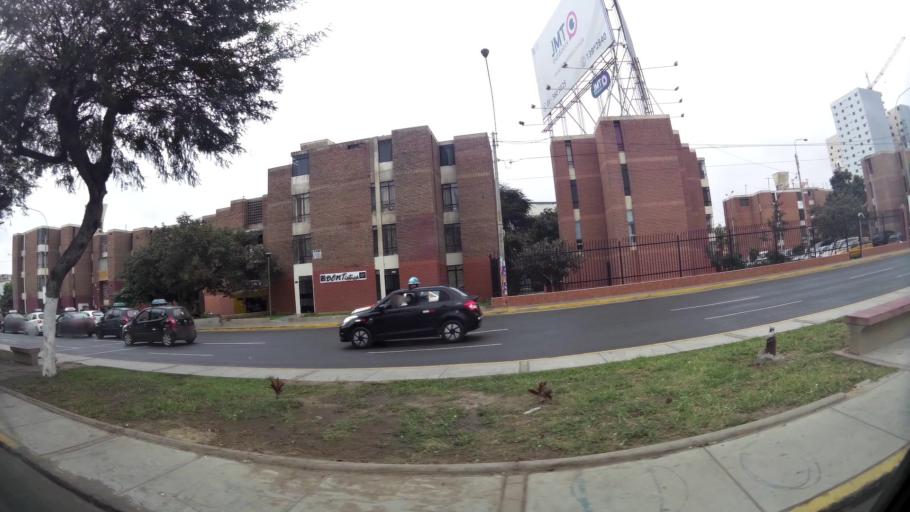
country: PE
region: La Libertad
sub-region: Provincia de Trujillo
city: Trujillo
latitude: -8.1120
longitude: -79.0340
